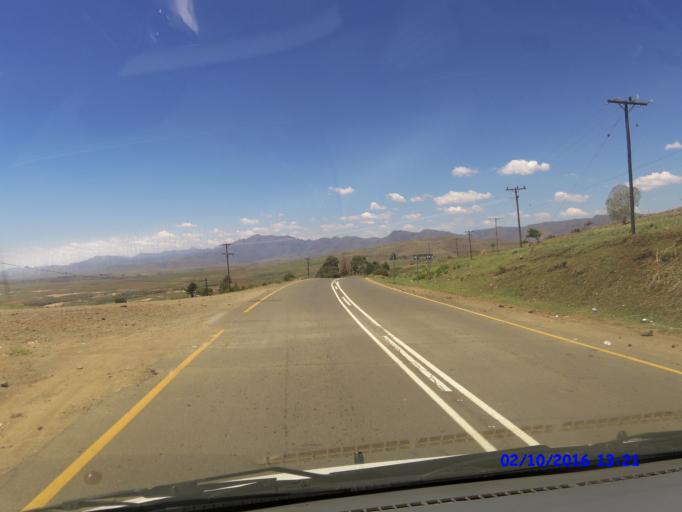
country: LS
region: Maseru
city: Nako
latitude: -29.4185
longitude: 27.7141
